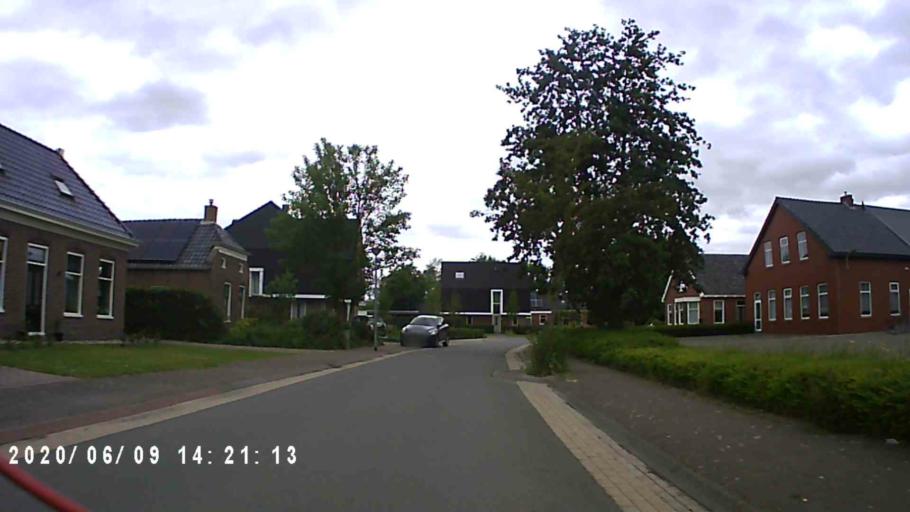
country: NL
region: Groningen
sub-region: Gemeente Bedum
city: Bedum
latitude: 53.2966
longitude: 6.5921
